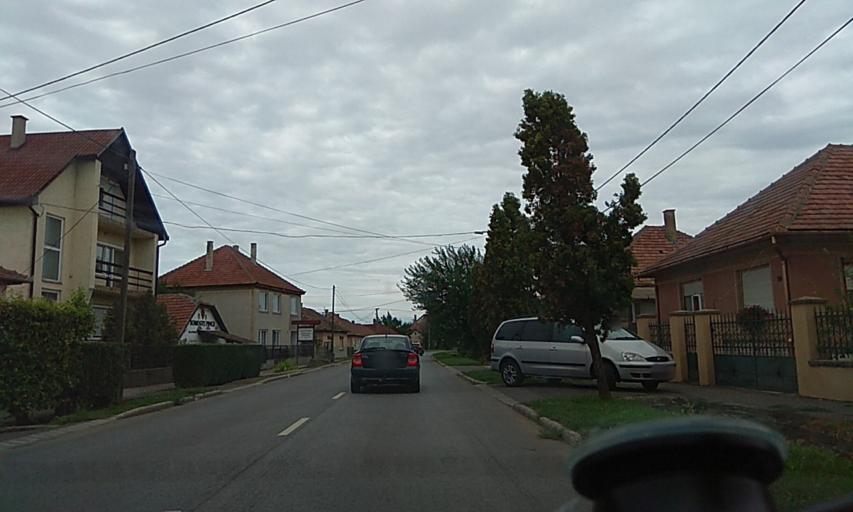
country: HU
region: Borsod-Abauj-Zemplen
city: Tarcal
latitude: 48.1314
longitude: 21.3432
